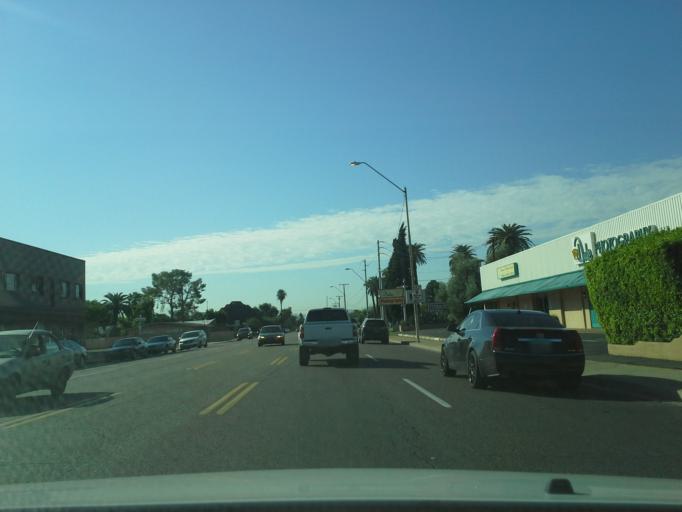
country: US
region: Arizona
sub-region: Maricopa County
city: Phoenix
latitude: 33.4802
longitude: -112.0831
